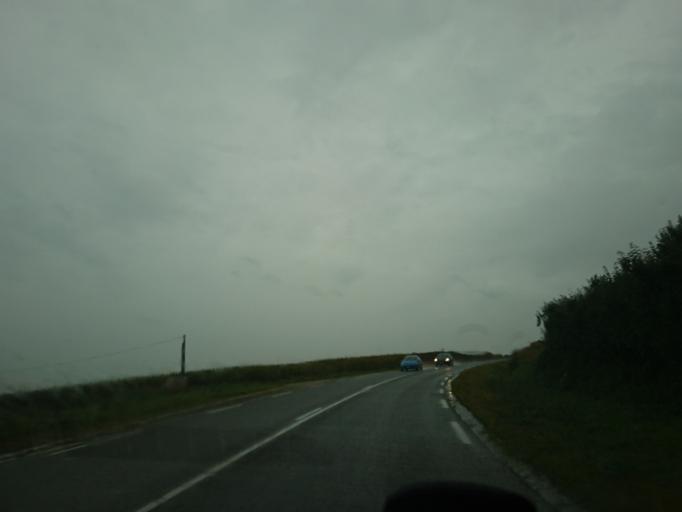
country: FR
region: Brittany
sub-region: Departement du Finistere
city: Plouguerneau
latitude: 48.6126
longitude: -4.4847
